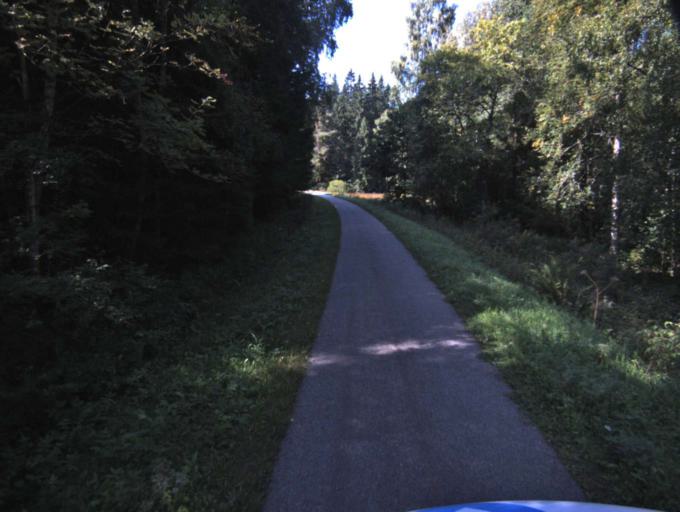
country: SE
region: Vaestra Goetaland
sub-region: Ulricehamns Kommun
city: Ulricehamn
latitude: 57.8377
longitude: 13.3336
